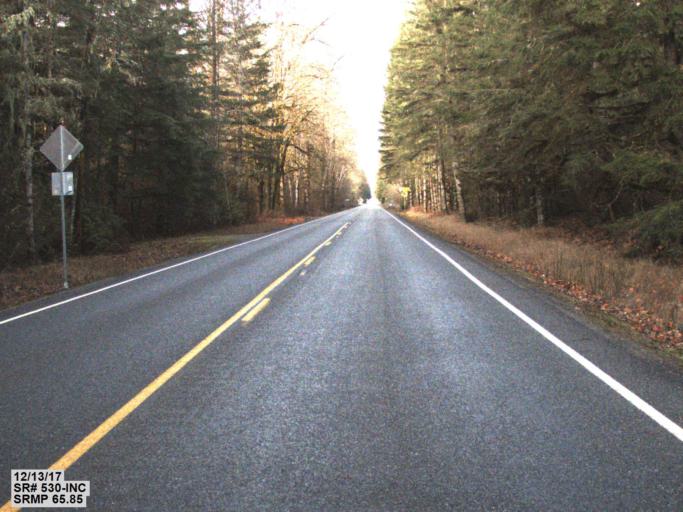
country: US
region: Washington
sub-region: Snohomish County
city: Darrington
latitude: 48.4631
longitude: -121.5861
